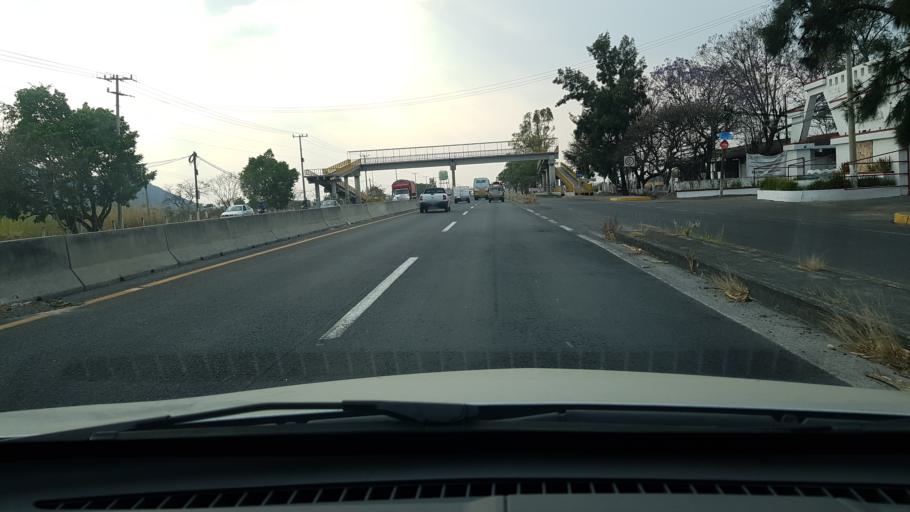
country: MX
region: Morelos
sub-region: Ayala
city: Unidad Habitacional Mariano Matamoros
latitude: 18.7481
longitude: -98.8462
